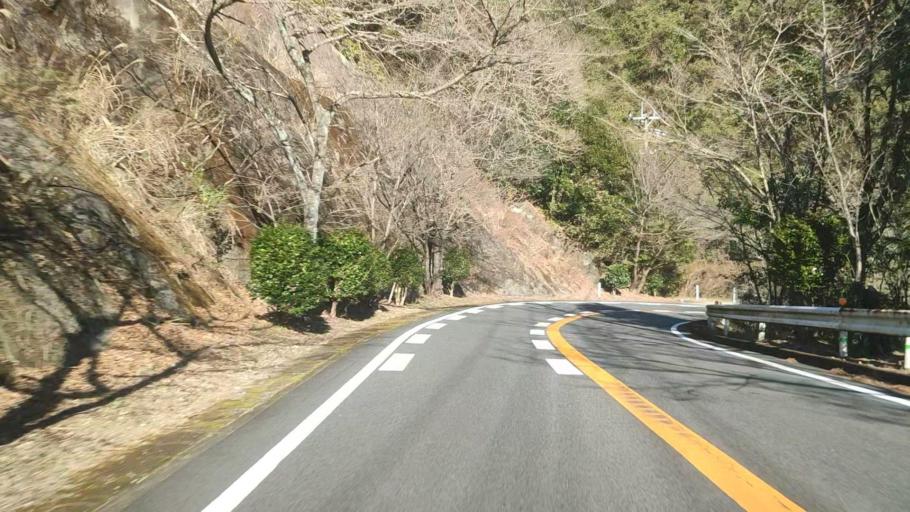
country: JP
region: Miyazaki
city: Nobeoka
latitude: 32.6317
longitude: 131.7355
